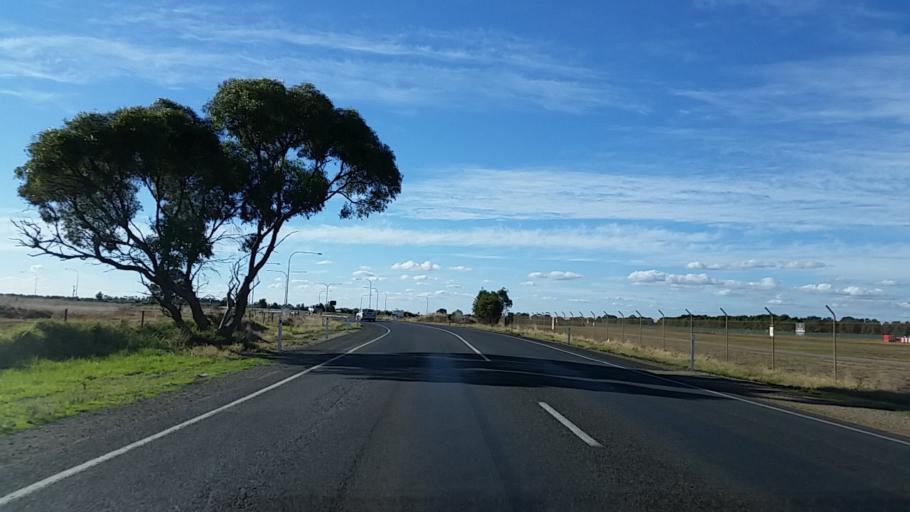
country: AU
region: South Australia
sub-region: Playford
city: Virginia
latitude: -34.6951
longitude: 138.6142
